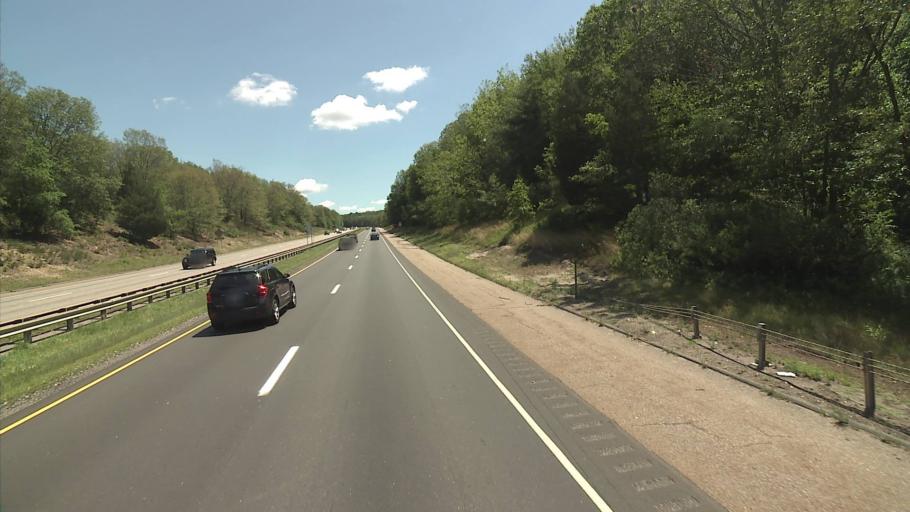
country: US
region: Connecticut
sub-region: New London County
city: Lisbon
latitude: 41.5853
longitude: -72.0436
